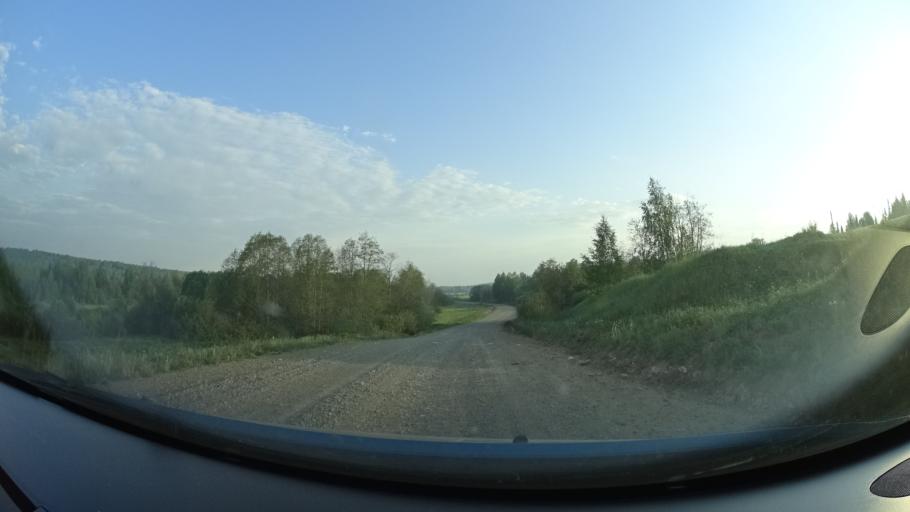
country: RU
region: Perm
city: Barda
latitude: 56.6935
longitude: 55.6828
